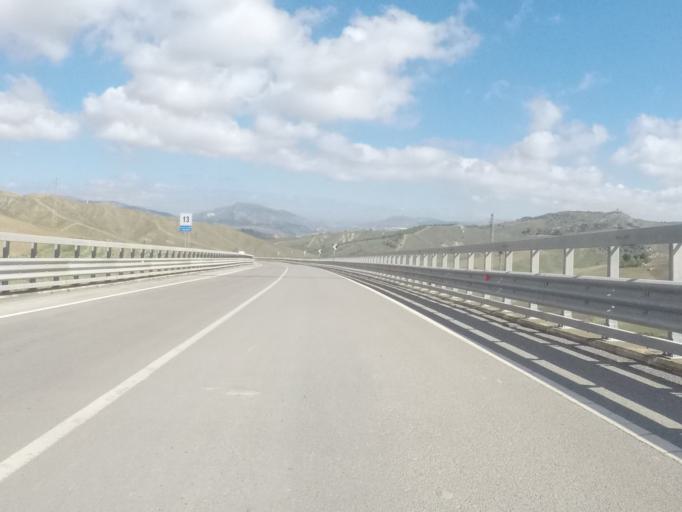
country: IT
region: Sicily
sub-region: Enna
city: Pietraperzia
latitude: 37.4268
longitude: 14.1225
